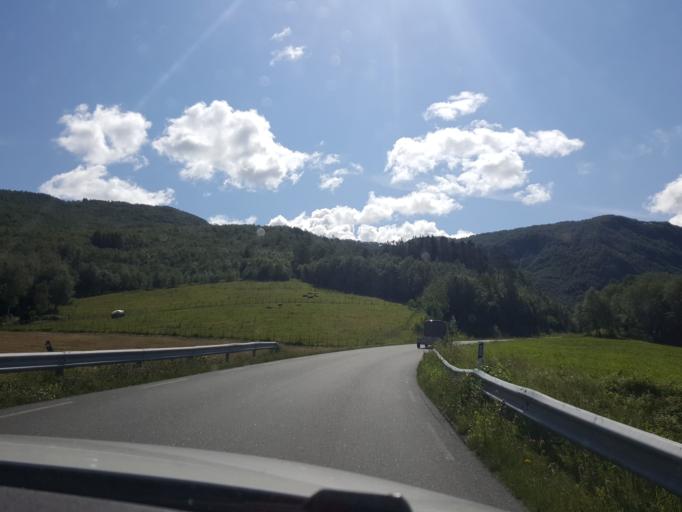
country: NO
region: Nordland
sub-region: Bodo
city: Loding
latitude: 67.1192
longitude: 15.0188
